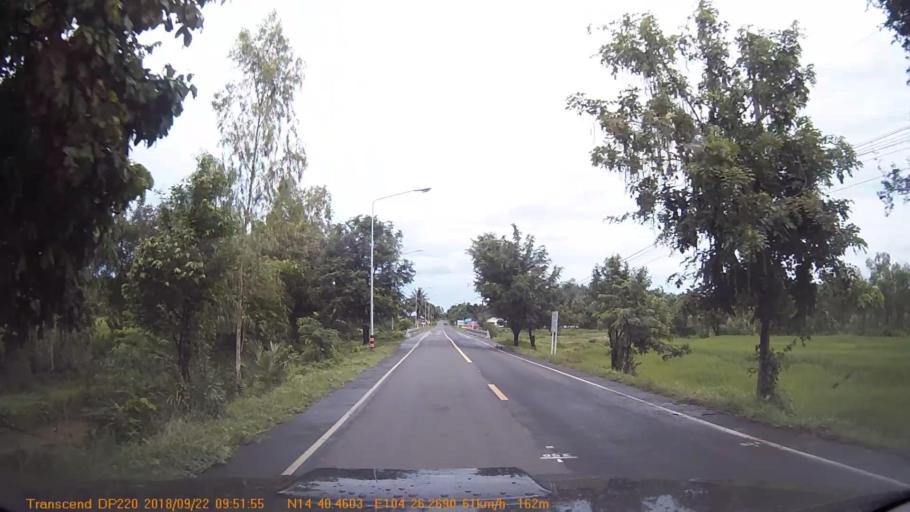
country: TH
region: Sisaket
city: Khun Han
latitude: 14.6744
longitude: 104.4378
